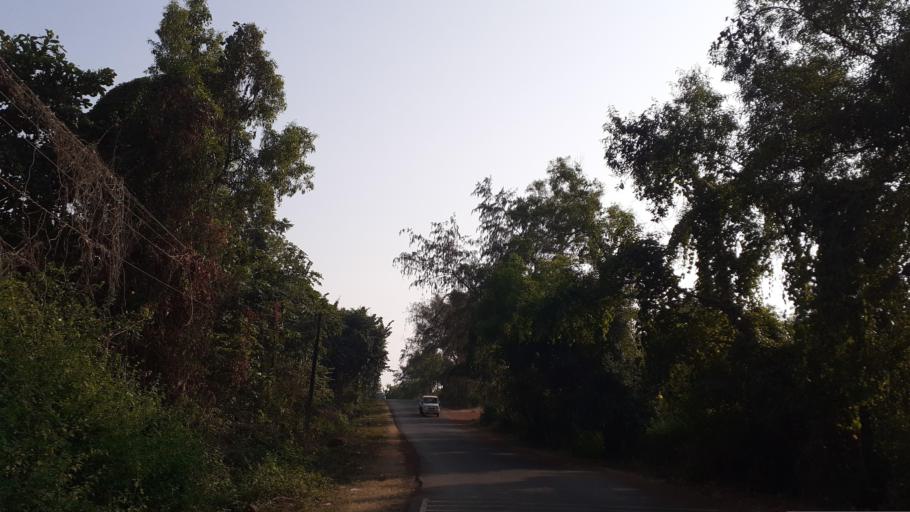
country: IN
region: Maharashtra
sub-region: Ratnagiri
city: Ratnagiri
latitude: 17.1429
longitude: 73.2695
